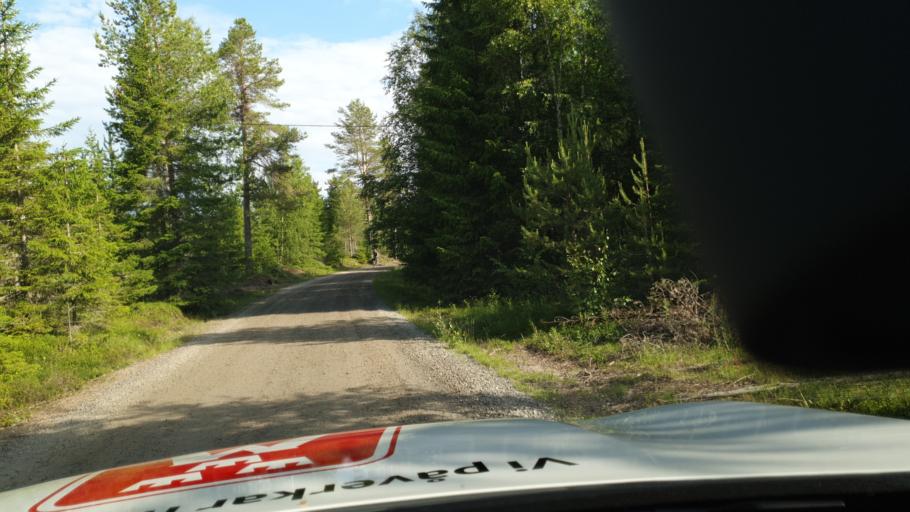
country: SE
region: Vaesterbotten
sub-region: Robertsfors Kommun
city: Robertsfors
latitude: 64.2137
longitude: 21.0783
